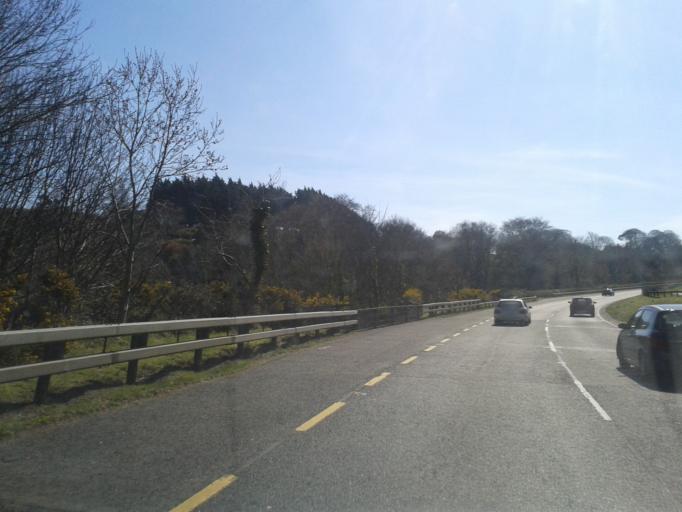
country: IE
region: Leinster
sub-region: Wicklow
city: Kilpedder
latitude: 53.1287
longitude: -6.1051
